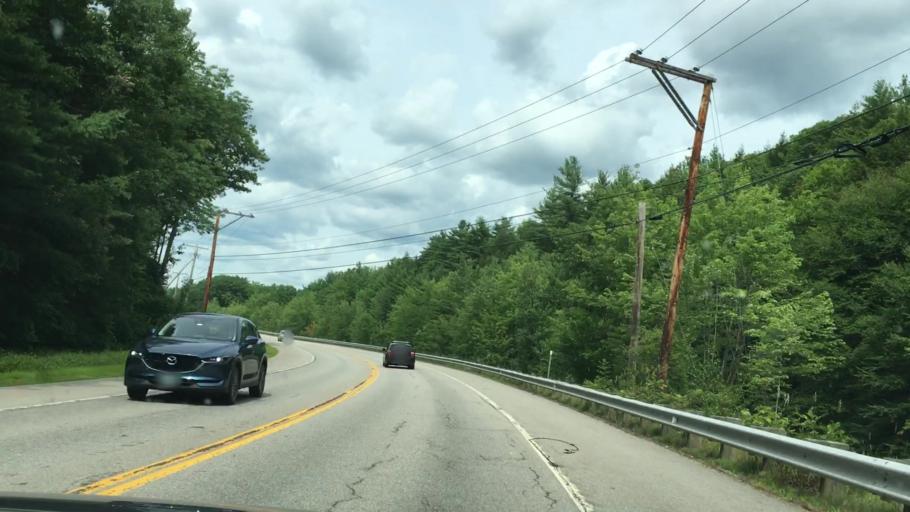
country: US
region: New Hampshire
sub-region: Hillsborough County
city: Peterborough
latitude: 42.8384
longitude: -71.9698
